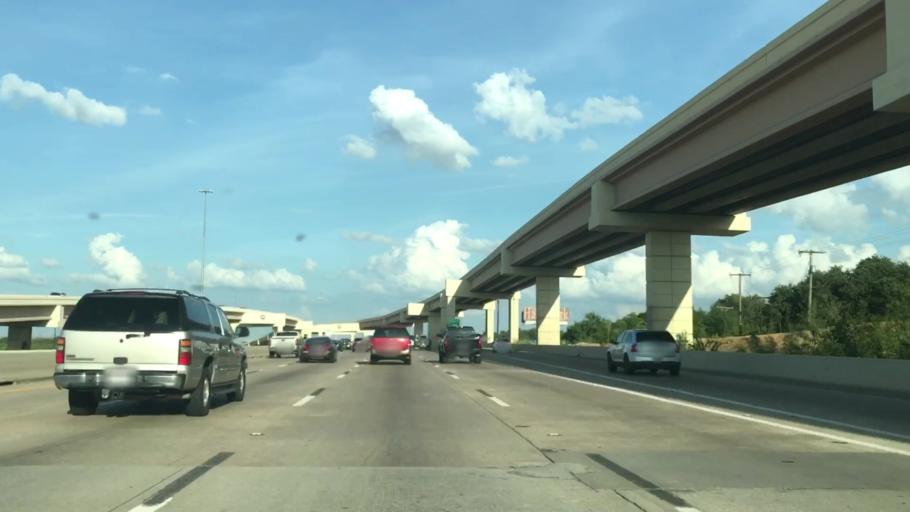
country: US
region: Texas
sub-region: Dallas County
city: Grand Prairie
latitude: 32.7593
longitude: -96.9760
